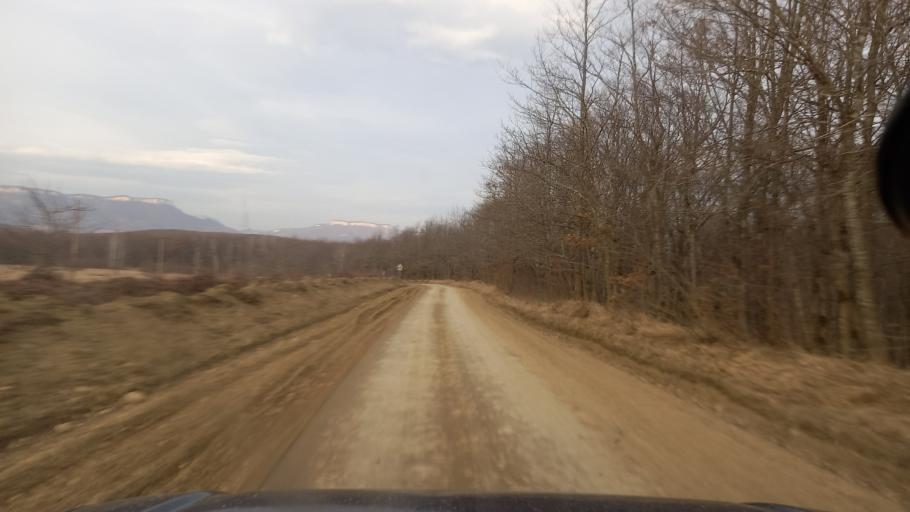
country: RU
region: Adygeya
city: Kamennomostskiy
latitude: 44.1584
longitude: 40.2435
